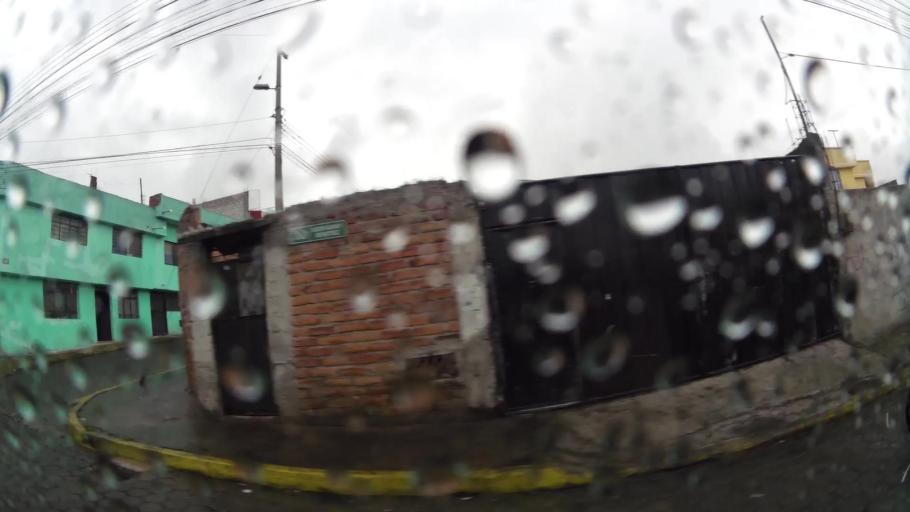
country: EC
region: Pichincha
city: Quito
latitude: -0.3219
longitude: -78.5527
